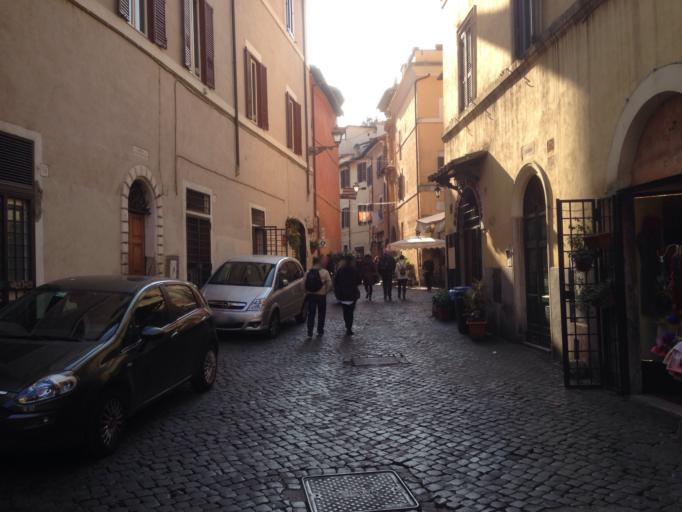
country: VA
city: Vatican City
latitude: 41.8905
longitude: 12.4690
